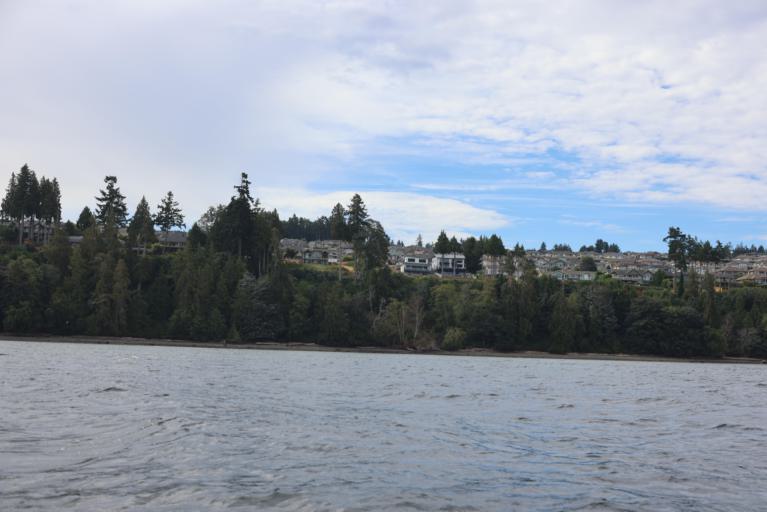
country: CA
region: British Columbia
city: Nanaimo
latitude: 49.2522
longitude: -124.0458
